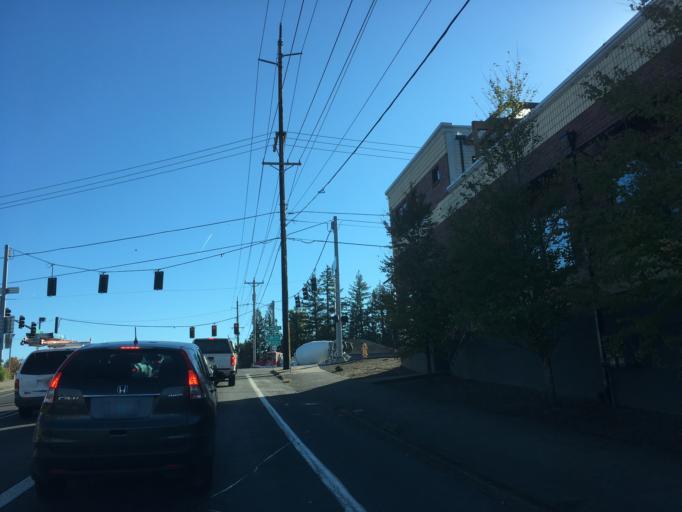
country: US
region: Oregon
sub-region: Multnomah County
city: Gresham
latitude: 45.4984
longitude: -122.4140
